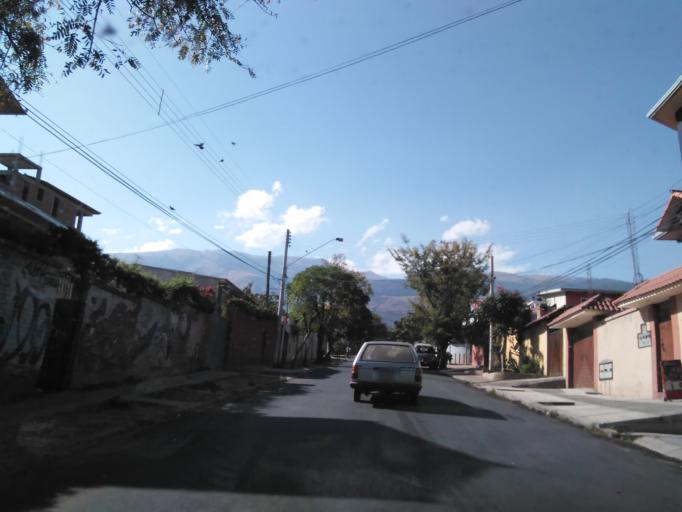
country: BO
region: Cochabamba
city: Cochabamba
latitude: -17.3596
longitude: -66.1662
